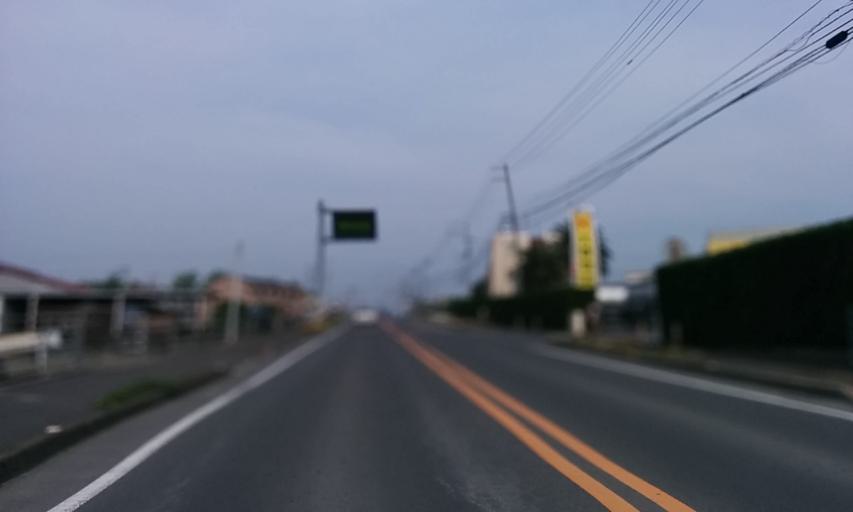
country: JP
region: Ehime
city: Kawanoecho
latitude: 33.9672
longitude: 133.4850
